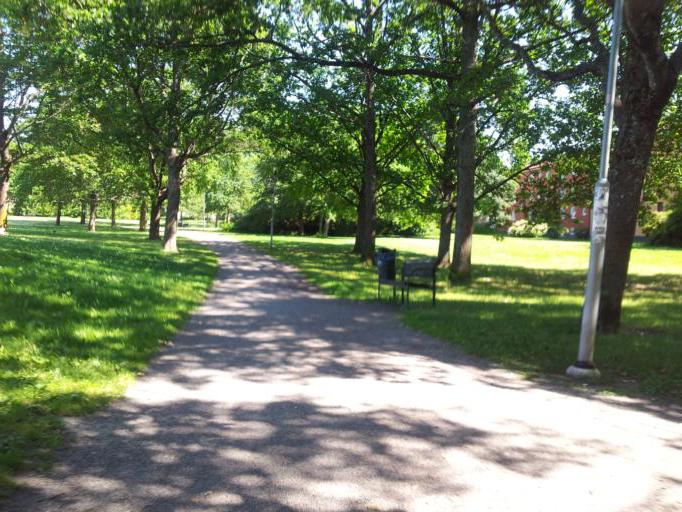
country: SE
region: Uppsala
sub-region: Uppsala Kommun
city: Uppsala
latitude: 59.8682
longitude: 17.6731
